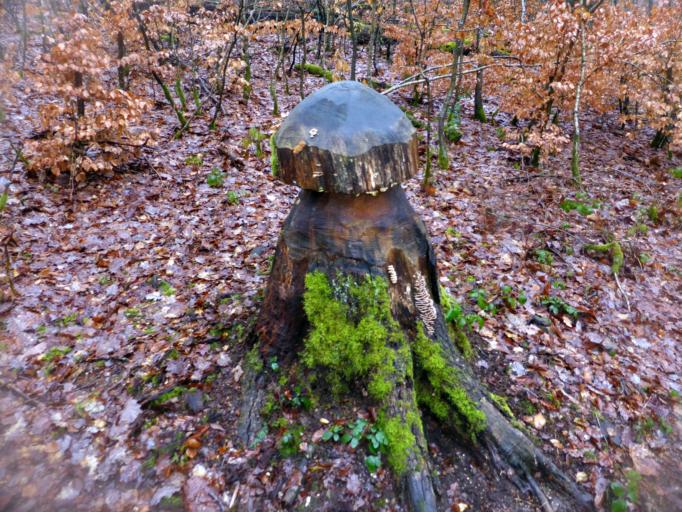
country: LU
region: Diekirch
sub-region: Canton de Redange
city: Ell
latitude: 49.7834
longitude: 5.8312
